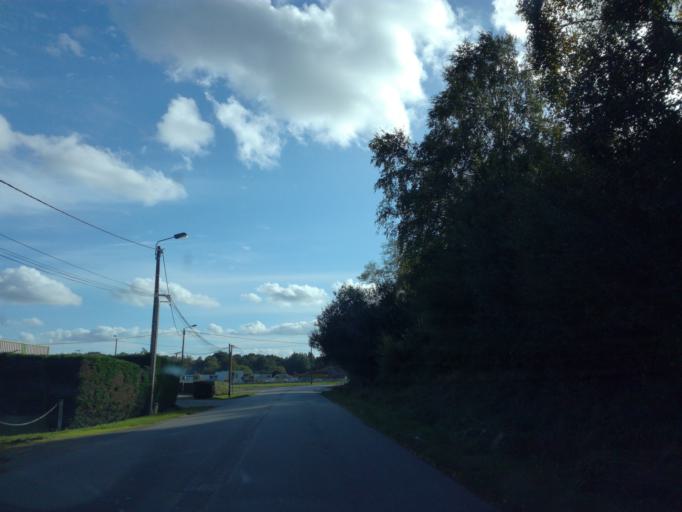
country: FR
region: Brittany
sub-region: Departement du Morbihan
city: Le Sourn
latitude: 48.0388
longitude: -2.9653
